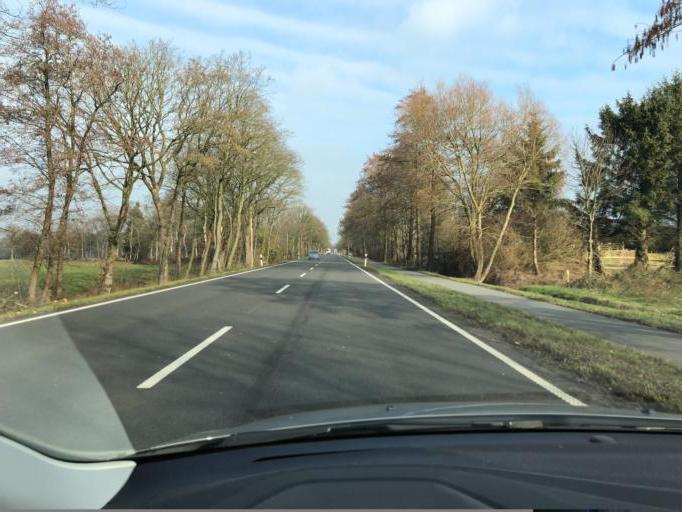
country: DE
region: Lower Saxony
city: Hesel
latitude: 53.3222
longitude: 7.6000
